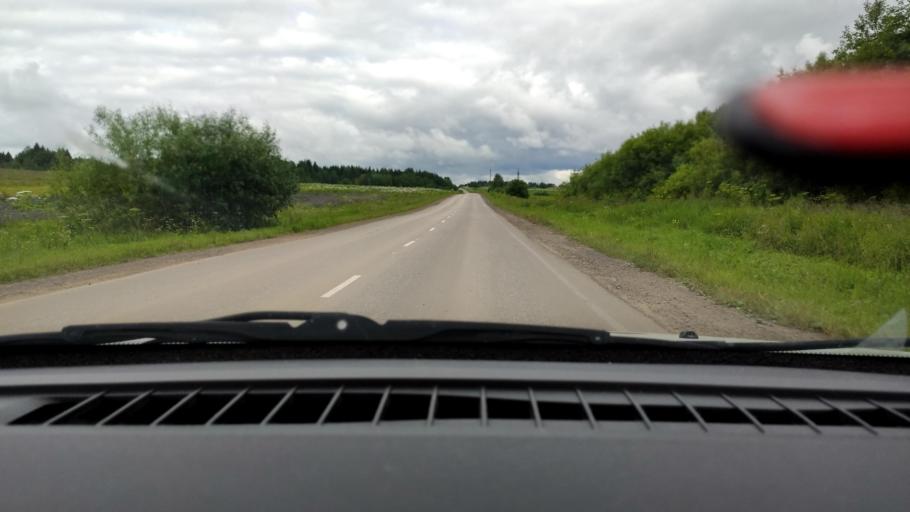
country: RU
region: Perm
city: Chaykovskaya
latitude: 58.1206
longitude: 55.5706
